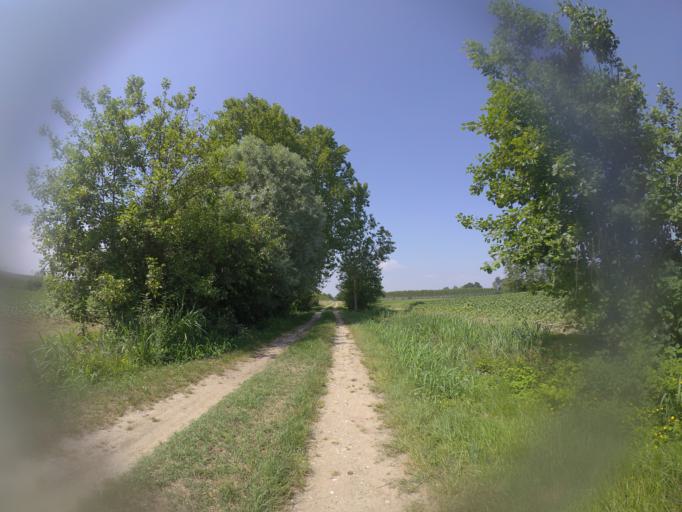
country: IT
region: Friuli Venezia Giulia
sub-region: Provincia di Udine
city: Bertiolo
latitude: 45.9259
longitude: 13.0259
